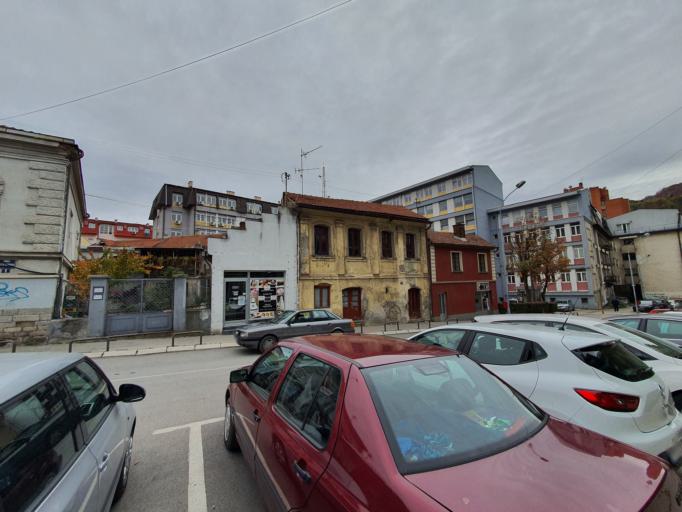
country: RS
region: Central Serbia
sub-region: Zlatiborski Okrug
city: Uzice
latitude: 43.8570
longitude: 19.8416
